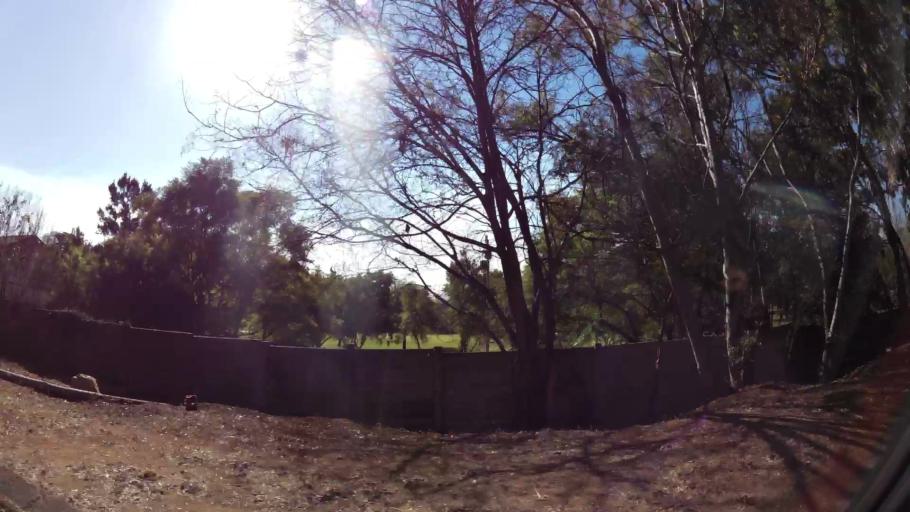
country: ZA
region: Gauteng
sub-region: City of Johannesburg Metropolitan Municipality
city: Roodepoort
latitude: -26.1204
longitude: 27.9655
